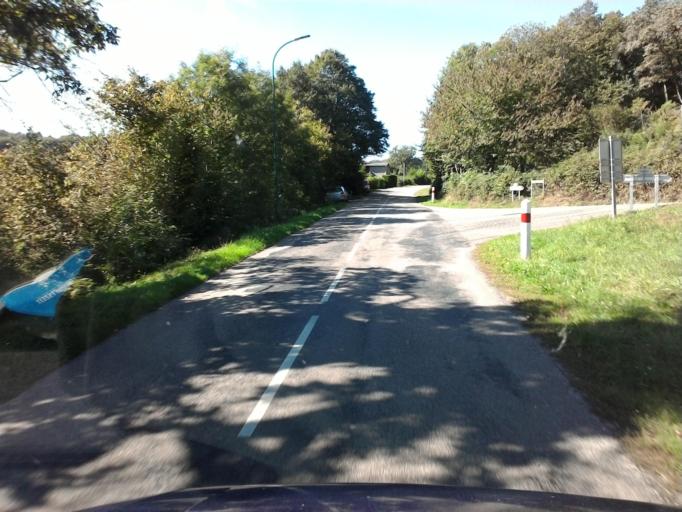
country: FR
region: Bourgogne
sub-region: Departement de la Nievre
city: Lormes
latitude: 47.2650
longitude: 3.8521
